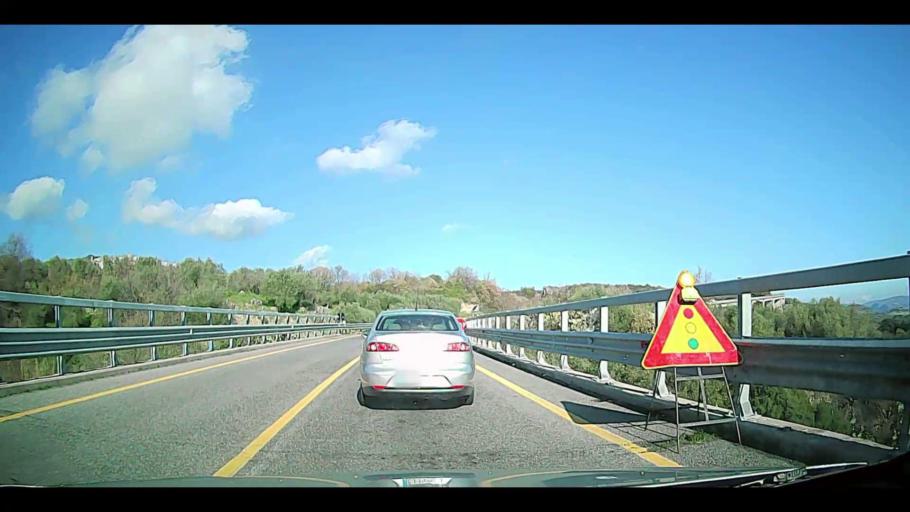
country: IT
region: Calabria
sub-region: Provincia di Crotone
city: Caccuri
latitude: 39.2212
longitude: 16.7938
